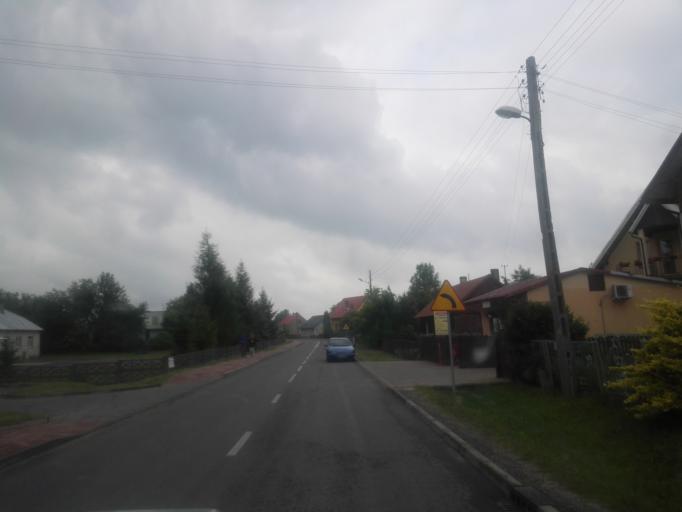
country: PL
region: Silesian Voivodeship
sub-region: Powiat czestochowski
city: Olsztyn
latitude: 50.7260
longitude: 19.3308
